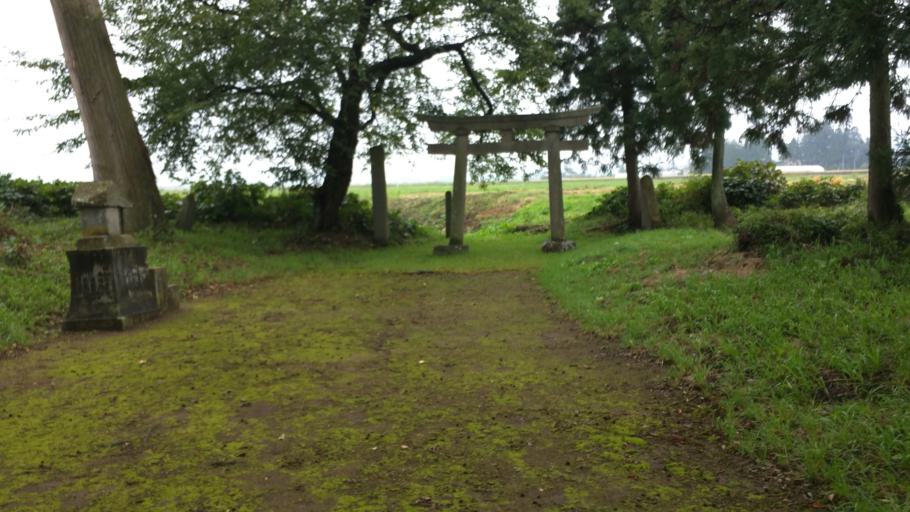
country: JP
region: Fukushima
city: Kitakata
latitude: 37.4809
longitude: 139.8347
